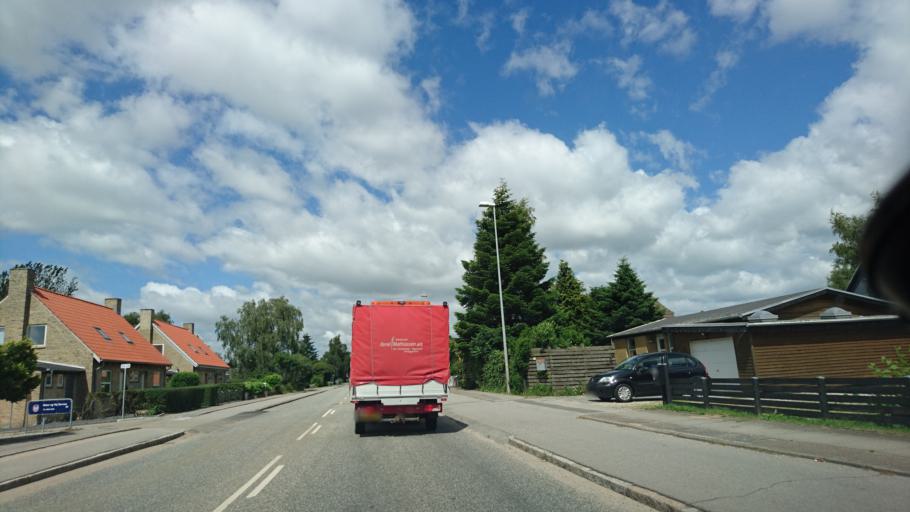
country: DK
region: Central Jutland
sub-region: Arhus Kommune
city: Lystrup
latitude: 56.2004
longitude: 10.2373
